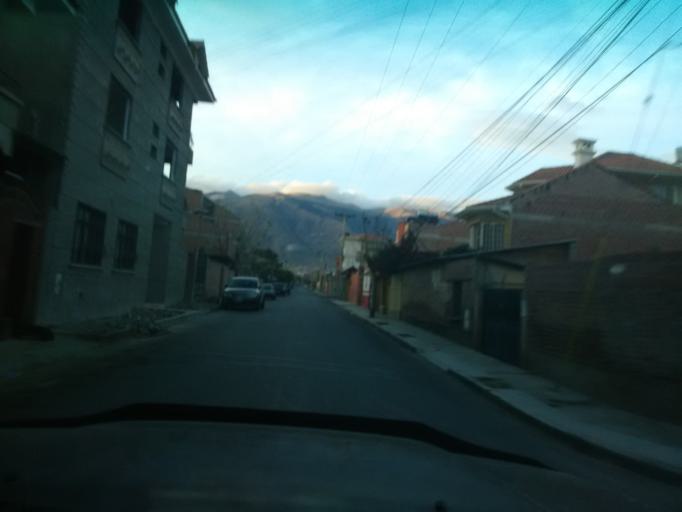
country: BO
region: Cochabamba
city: Cochabamba
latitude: -17.3750
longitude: -66.1920
